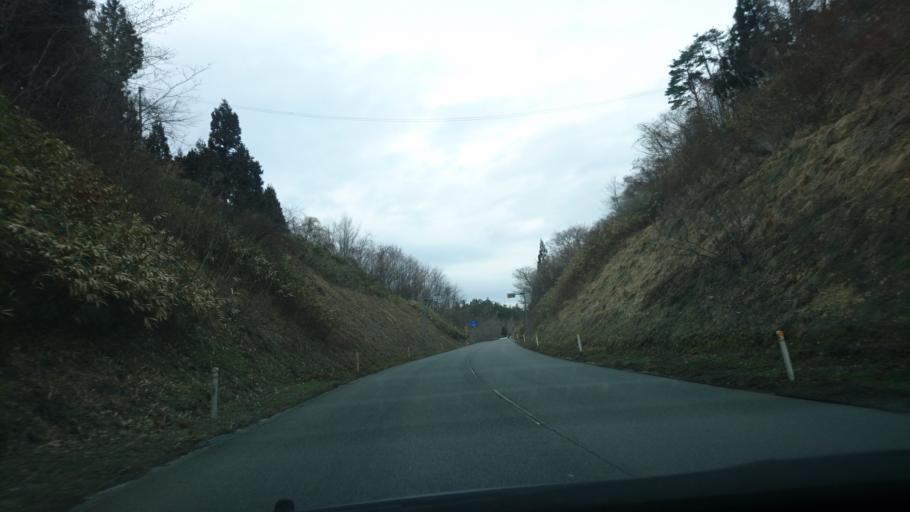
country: JP
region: Iwate
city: Ichinoseki
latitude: 38.9720
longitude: 141.3561
